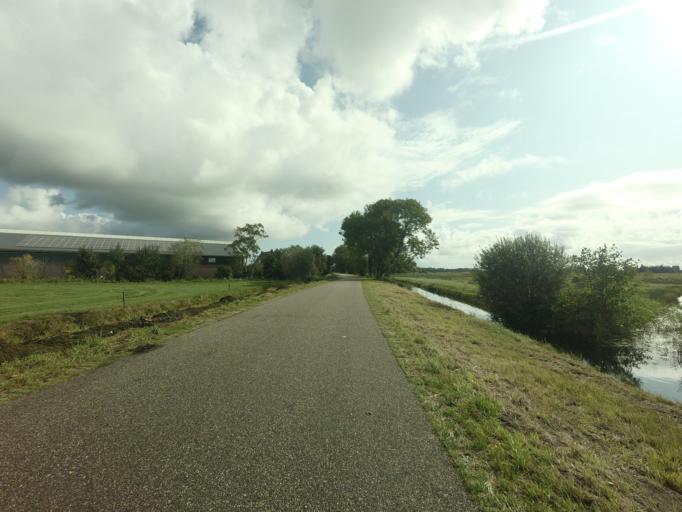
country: NL
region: Friesland
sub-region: Gemeente Tytsjerksteradiel
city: Garyp
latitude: 53.1495
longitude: 5.9378
